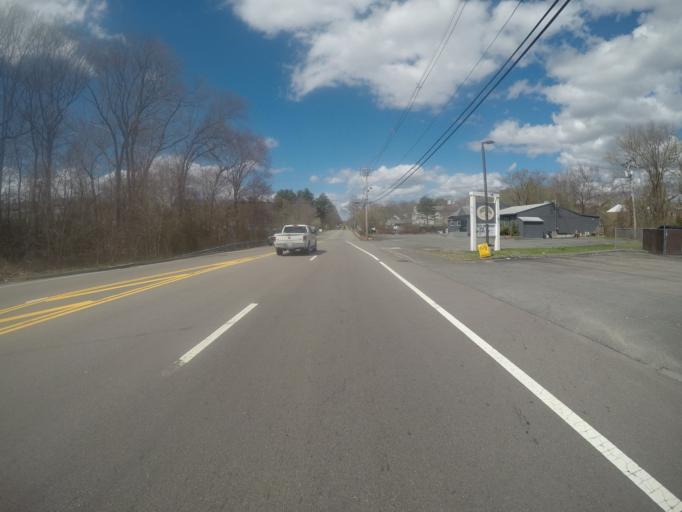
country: US
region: Massachusetts
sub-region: Plymouth County
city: West Bridgewater
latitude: 42.0112
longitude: -71.0667
